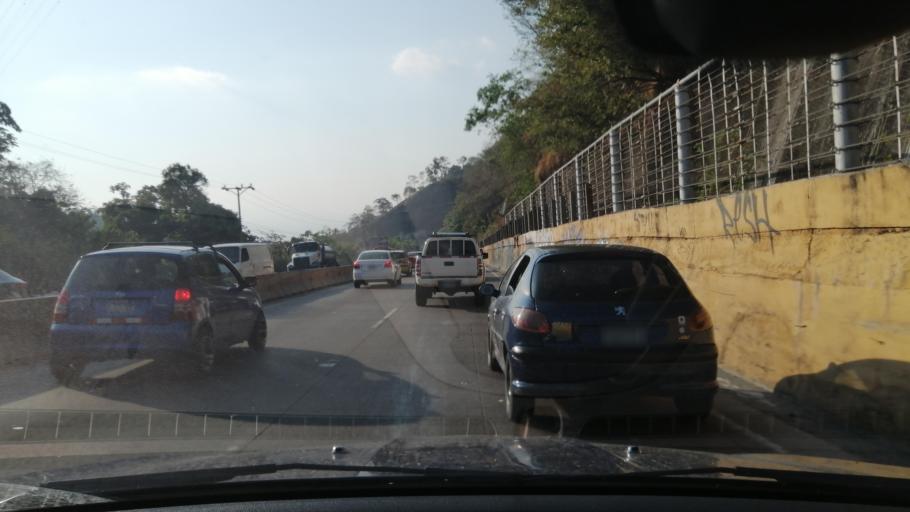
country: SV
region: La Libertad
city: Santa Tecla
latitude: 13.7008
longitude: -89.3353
